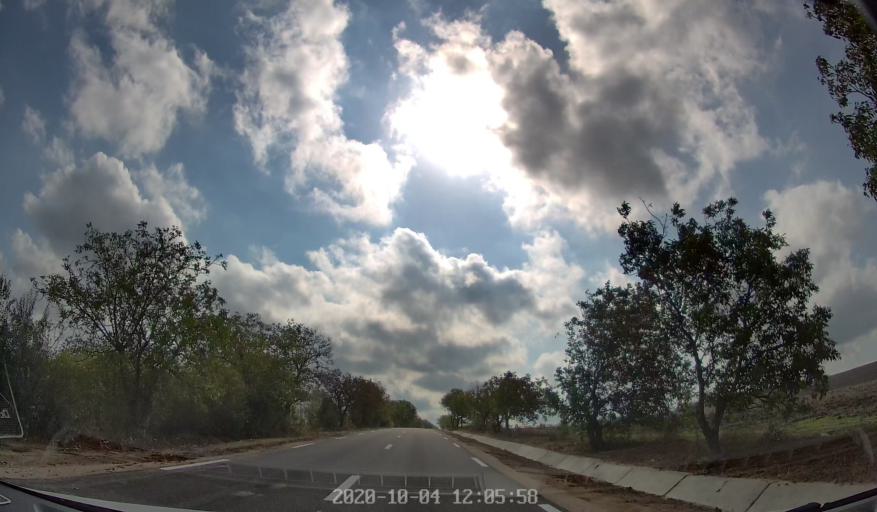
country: MD
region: Rezina
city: Saharna
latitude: 47.5883
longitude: 28.9540
